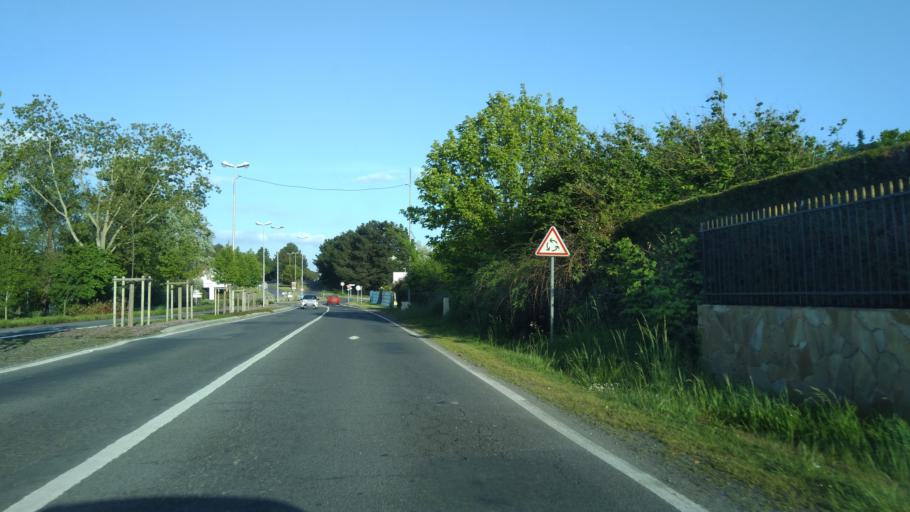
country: FR
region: Pays de la Loire
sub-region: Departement de la Loire-Atlantique
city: Pornichet
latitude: 47.2581
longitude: -2.3261
